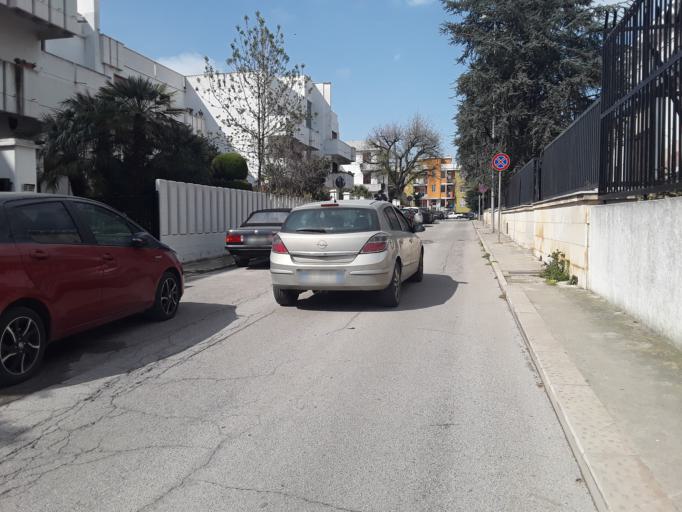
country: IT
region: Apulia
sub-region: Provincia di Bari
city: Ruvo di Puglia
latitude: 41.1211
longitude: 16.4772
